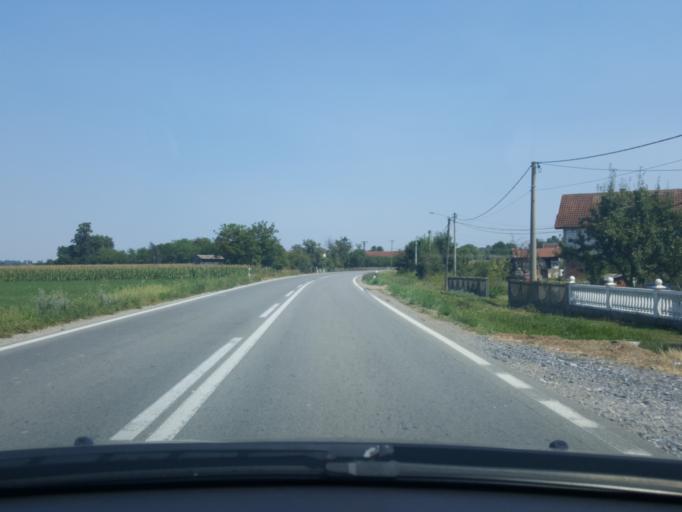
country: RS
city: Dublje
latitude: 44.7549
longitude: 19.5458
